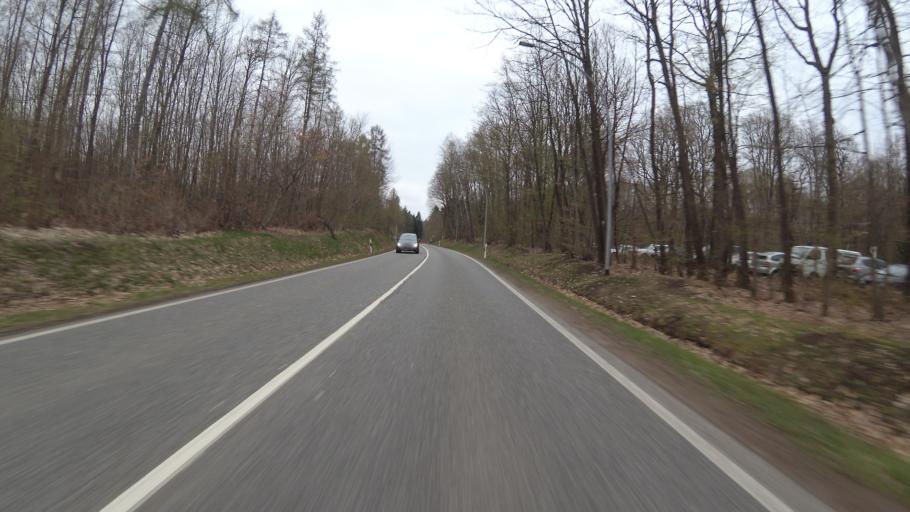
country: DE
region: Saarland
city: Sankt Ingbert
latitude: 49.2911
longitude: 7.1126
